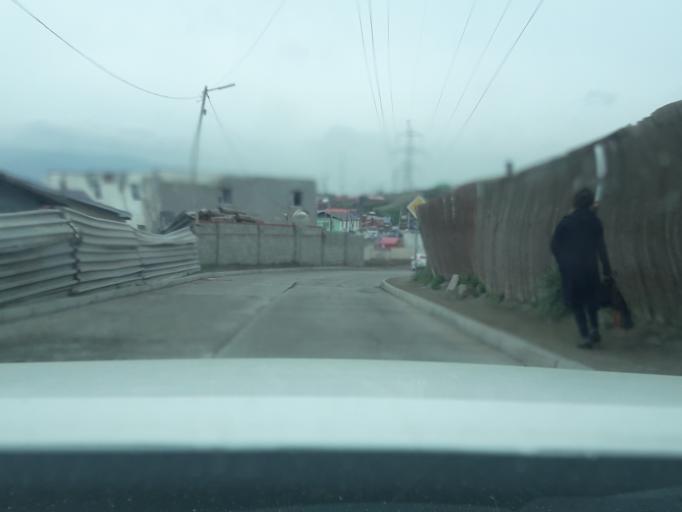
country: MN
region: Ulaanbaatar
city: Ulaanbaatar
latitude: 47.9477
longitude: 106.9040
